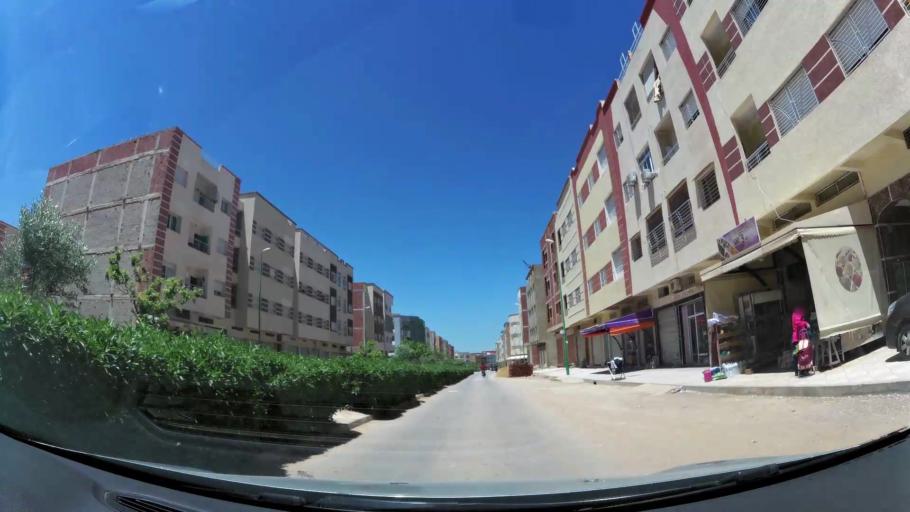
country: MA
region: Meknes-Tafilalet
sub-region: Meknes
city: Meknes
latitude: 33.8554
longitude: -5.5658
